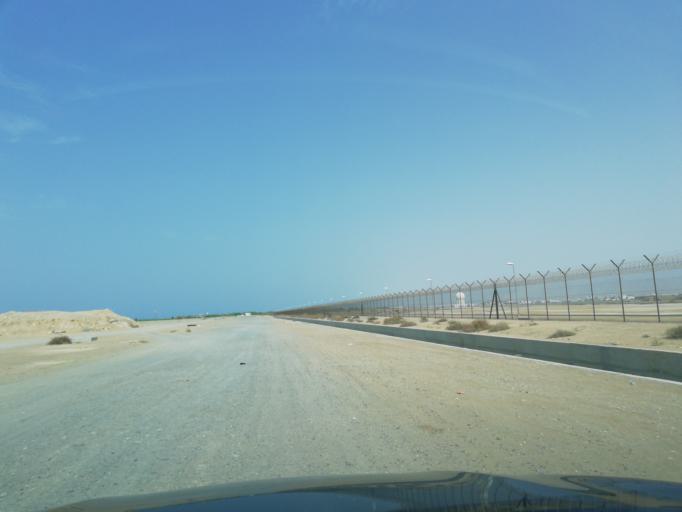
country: OM
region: Muhafazat Masqat
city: As Sib al Jadidah
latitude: 23.6151
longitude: 58.2783
